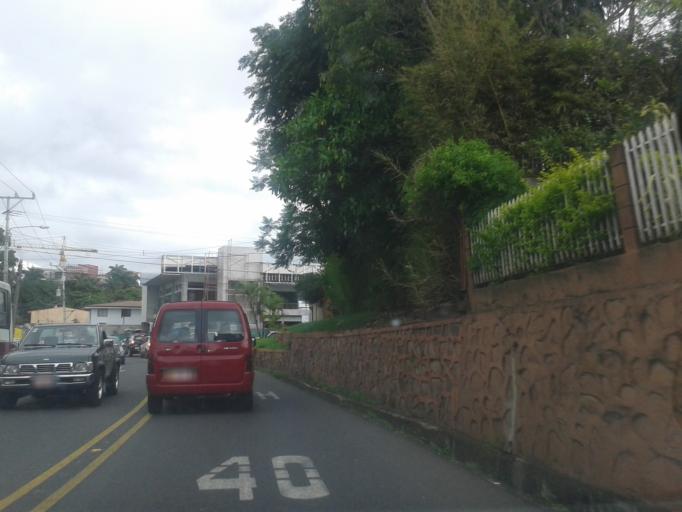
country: CR
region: San Jose
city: San Vicente de Moravia
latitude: 9.9627
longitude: -84.0612
